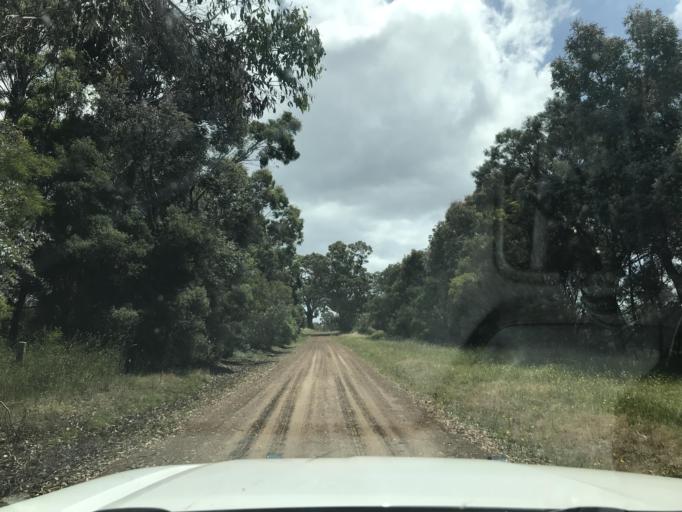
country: AU
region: South Australia
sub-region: Wattle Range
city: Penola
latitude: -37.2980
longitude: 141.4817
